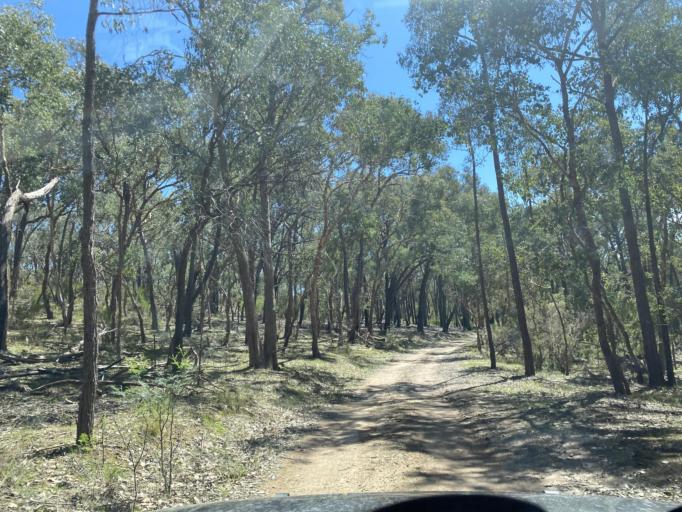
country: AU
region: Victoria
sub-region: Benalla
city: Benalla
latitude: -36.7020
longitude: 146.1518
